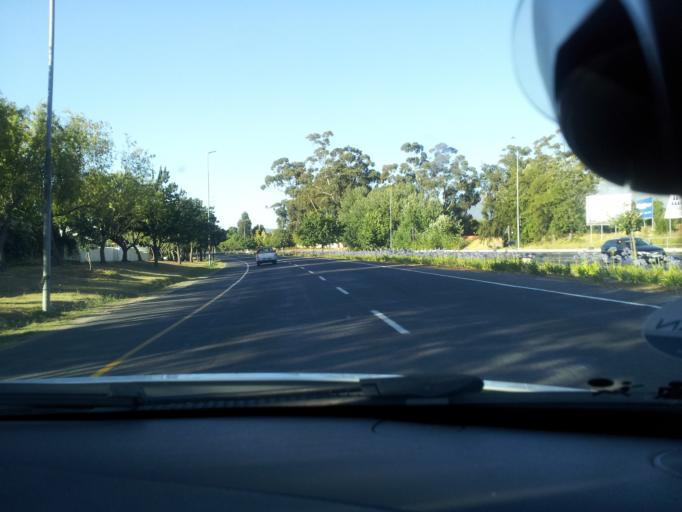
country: ZA
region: Western Cape
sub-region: Cape Winelands District Municipality
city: Stellenbosch
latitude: -33.9551
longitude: 18.8556
